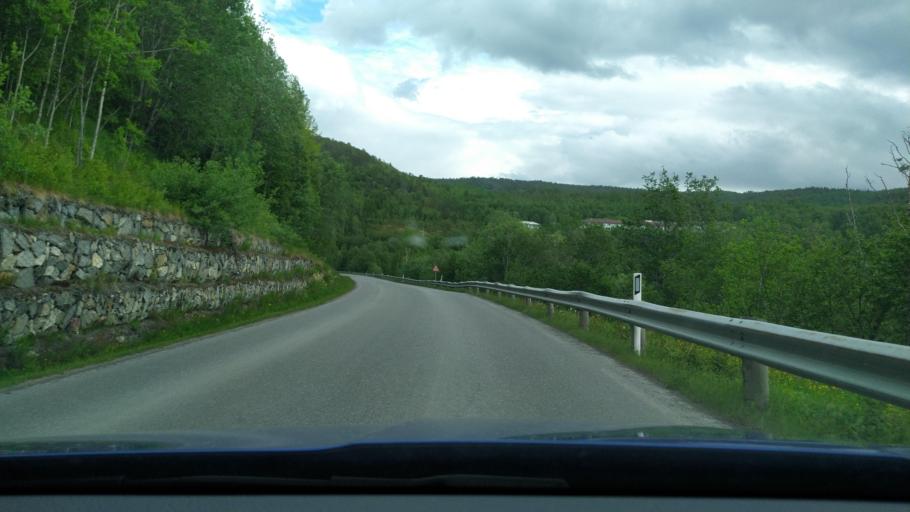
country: NO
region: Troms
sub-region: Salangen
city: Sjovegan
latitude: 68.8668
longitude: 17.8552
